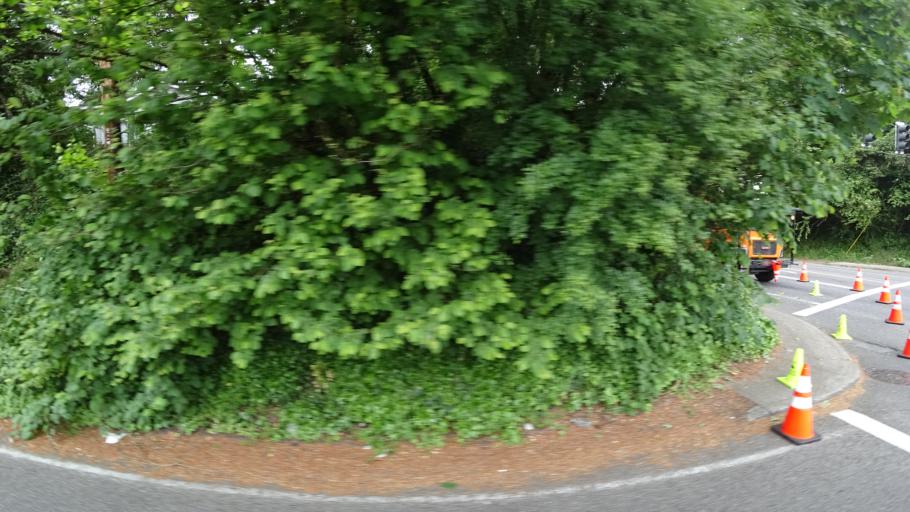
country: US
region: Oregon
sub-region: Washington County
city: Garden Home-Whitford
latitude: 45.4674
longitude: -122.7231
